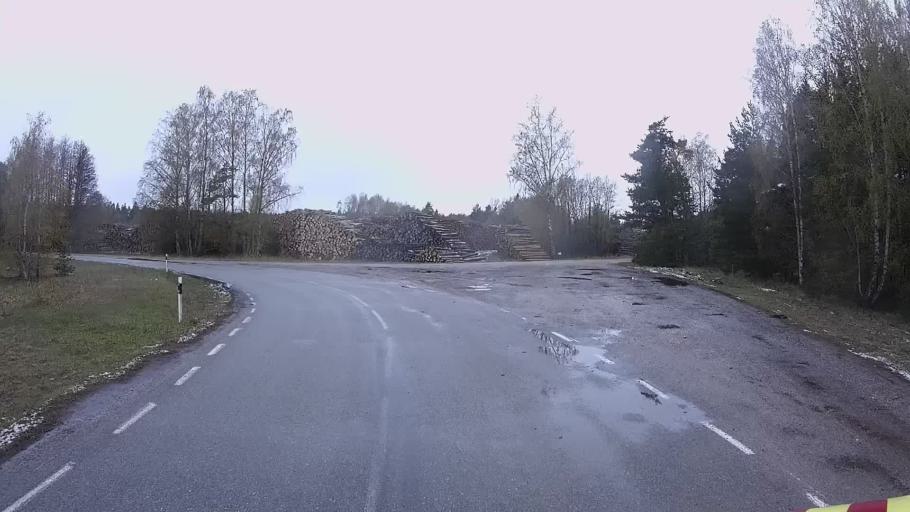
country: EE
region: Hiiumaa
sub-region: Kaerdla linn
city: Kardla
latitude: 59.0709
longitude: 22.6909
